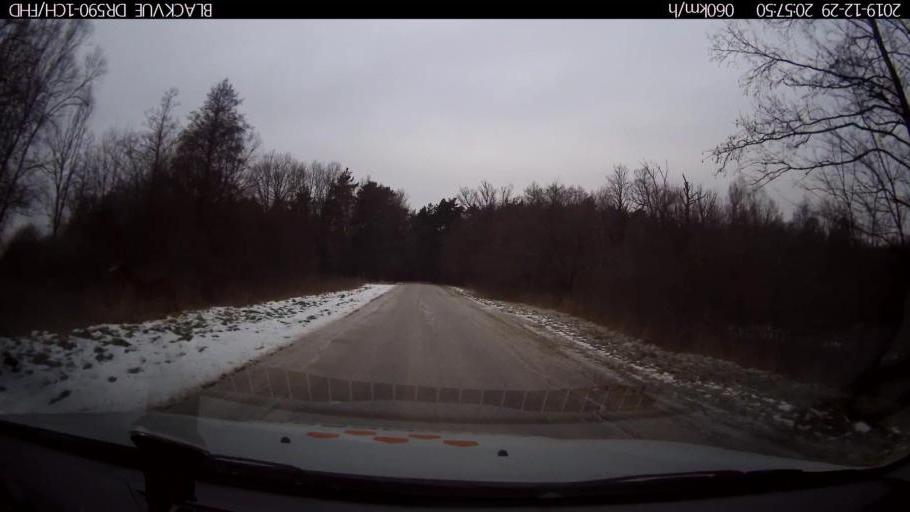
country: RU
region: Nizjnij Novgorod
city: Afonino
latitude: 56.1646
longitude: 43.9894
